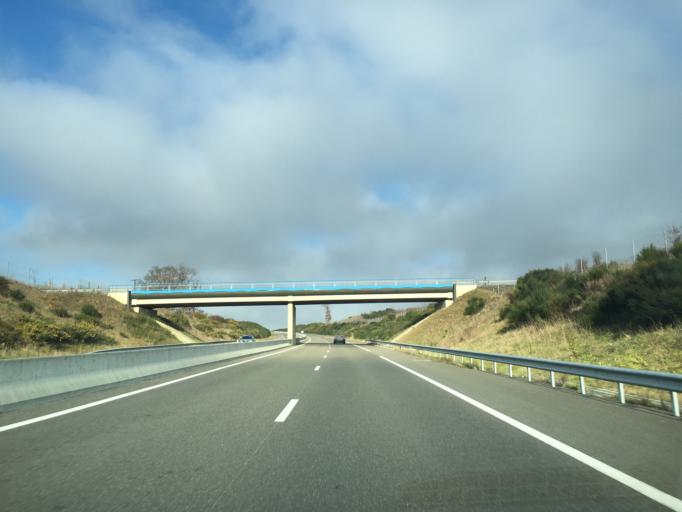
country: FR
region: Midi-Pyrenees
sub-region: Departement du Gers
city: Barcelonne-du-Gers
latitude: 43.7785
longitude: -0.2734
